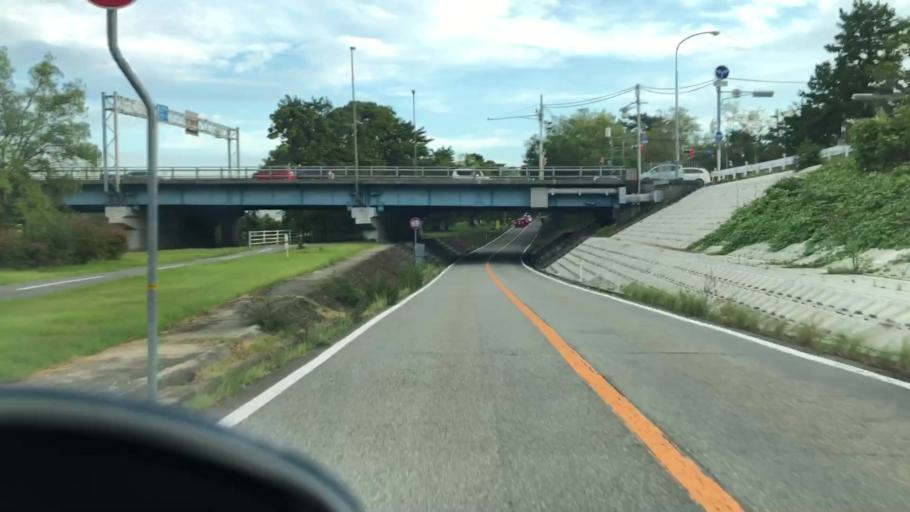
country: JP
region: Hyogo
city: Itami
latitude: 34.7653
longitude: 135.3724
